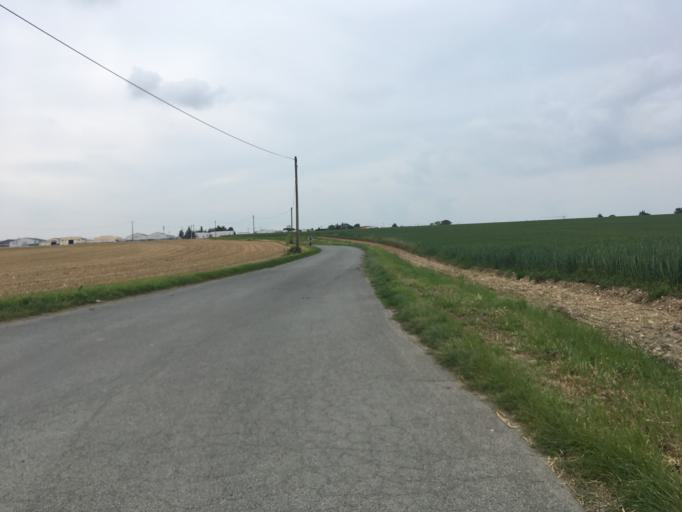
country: FR
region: Poitou-Charentes
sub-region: Departement de la Charente-Maritime
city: Aytre
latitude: 46.1462
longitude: -1.1214
